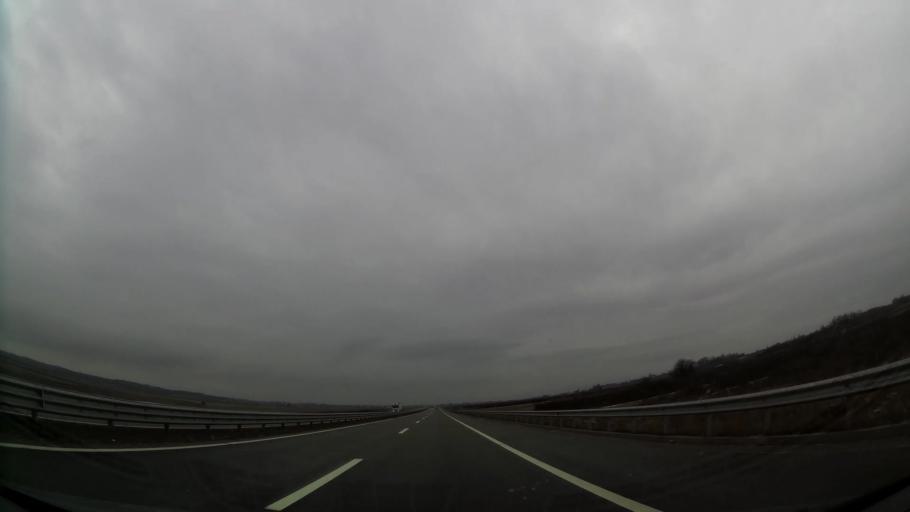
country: XK
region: Ferizaj
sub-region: Komuna e Ferizajt
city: Ferizaj
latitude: 42.4298
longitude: 21.2005
